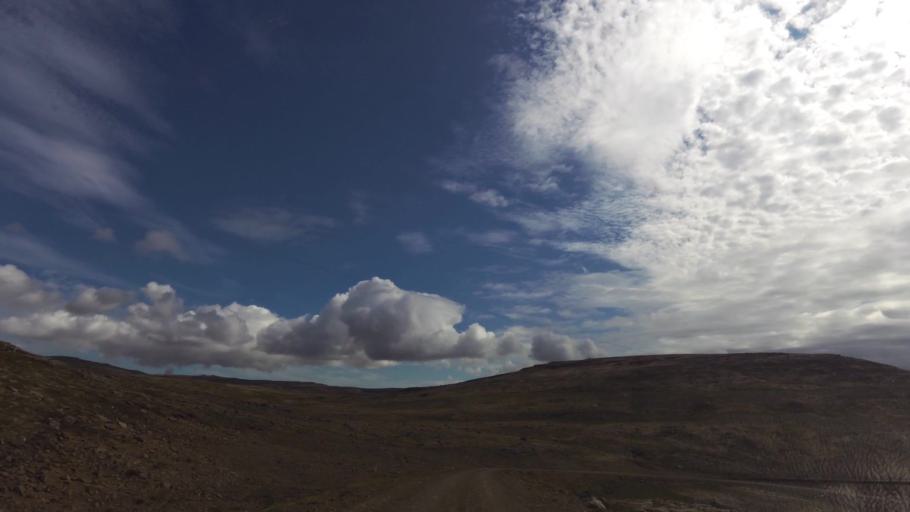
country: IS
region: West
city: Olafsvik
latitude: 65.6150
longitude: -24.3042
